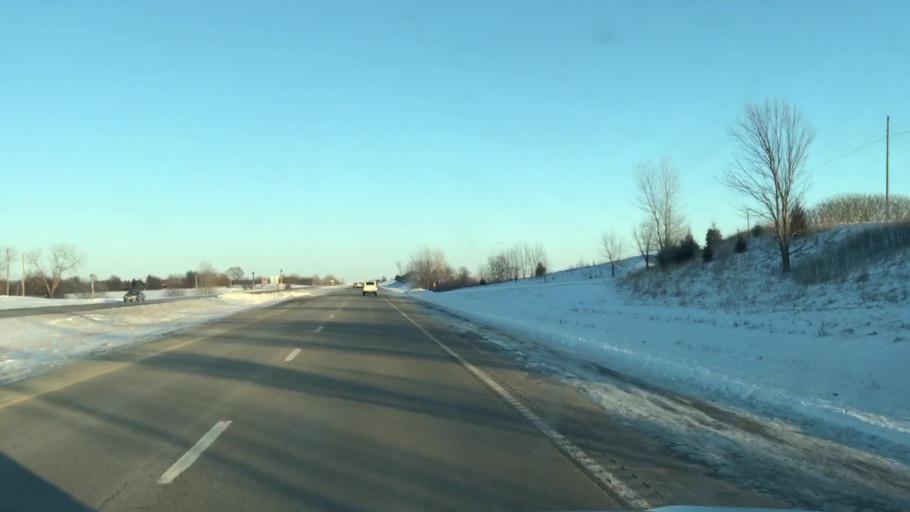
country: US
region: Missouri
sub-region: Clinton County
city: Gower
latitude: 39.7471
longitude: -94.6286
